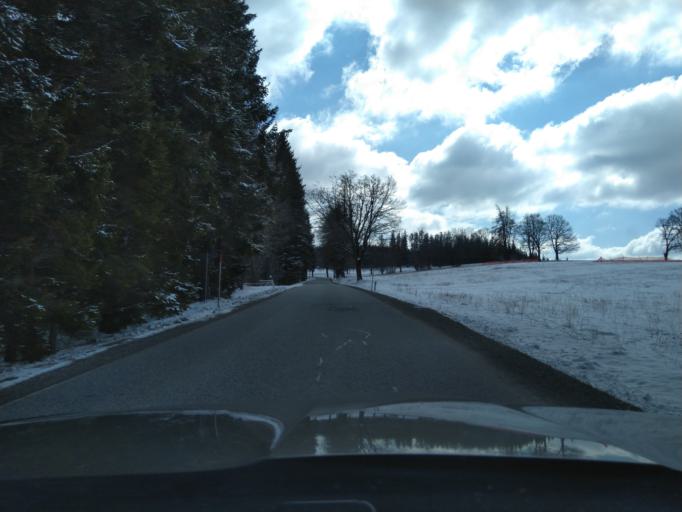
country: CZ
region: Jihocesky
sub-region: Okres Prachatice
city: Zdikov
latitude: 49.0469
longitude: 13.6702
